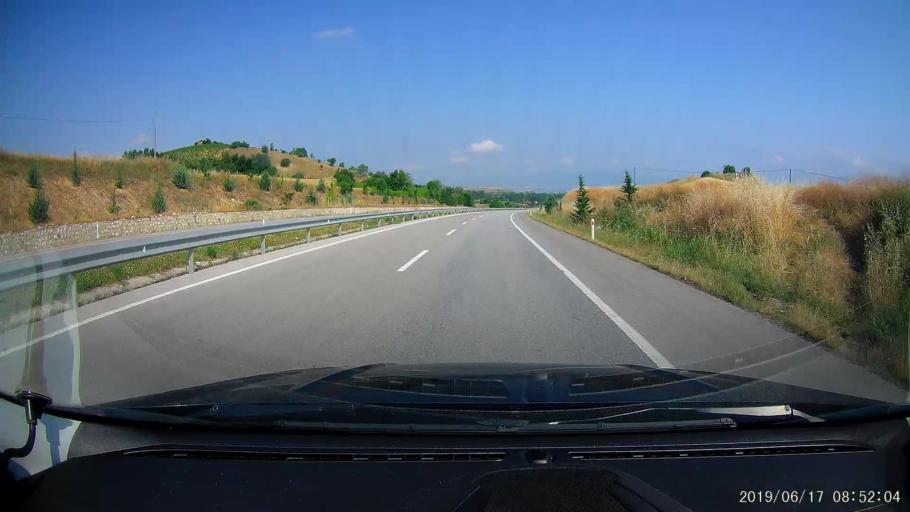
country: TR
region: Tokat
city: Erbaa
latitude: 40.6930
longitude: 36.5028
